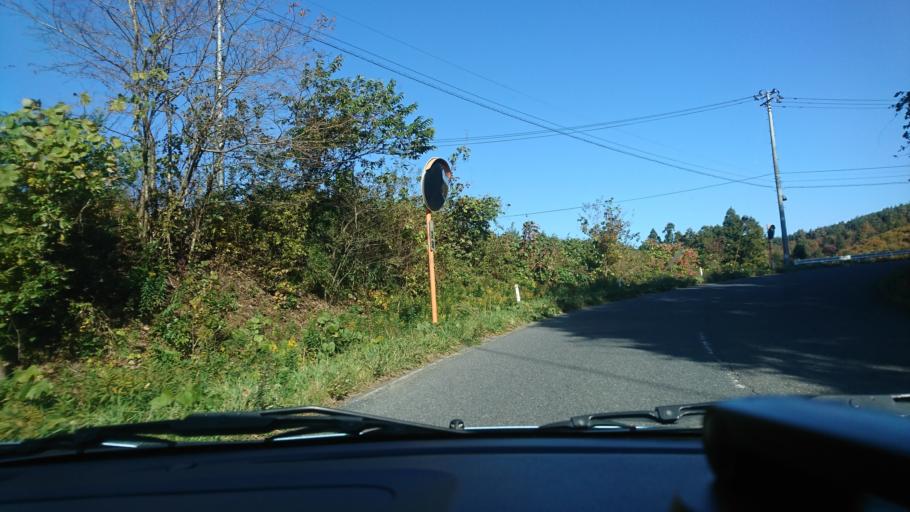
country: JP
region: Iwate
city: Ichinoseki
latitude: 38.7974
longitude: 141.2517
